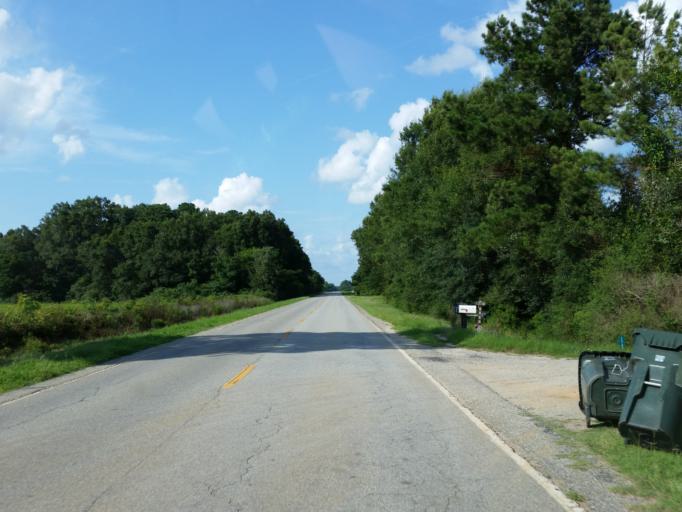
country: US
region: Georgia
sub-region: Lee County
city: Leesburg
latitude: 31.8284
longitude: -84.1035
